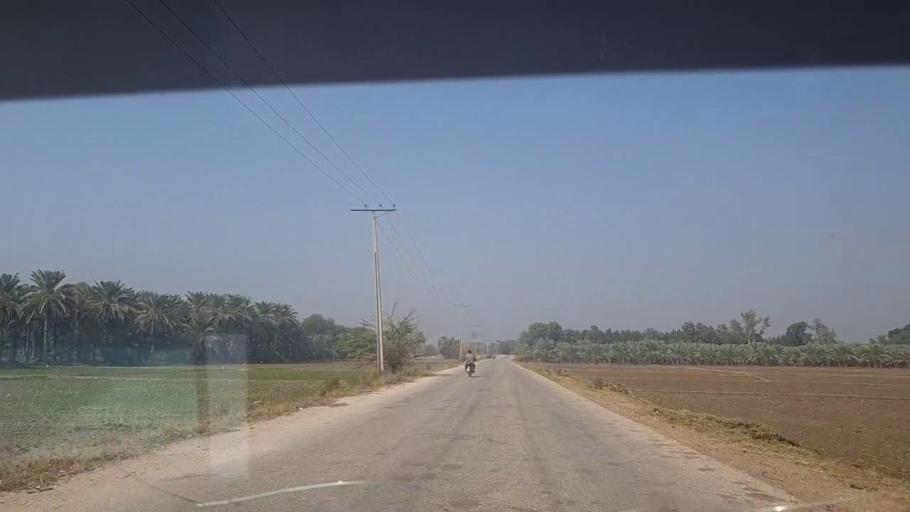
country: PK
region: Sindh
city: Kot Diji
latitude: 27.3682
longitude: 68.7016
